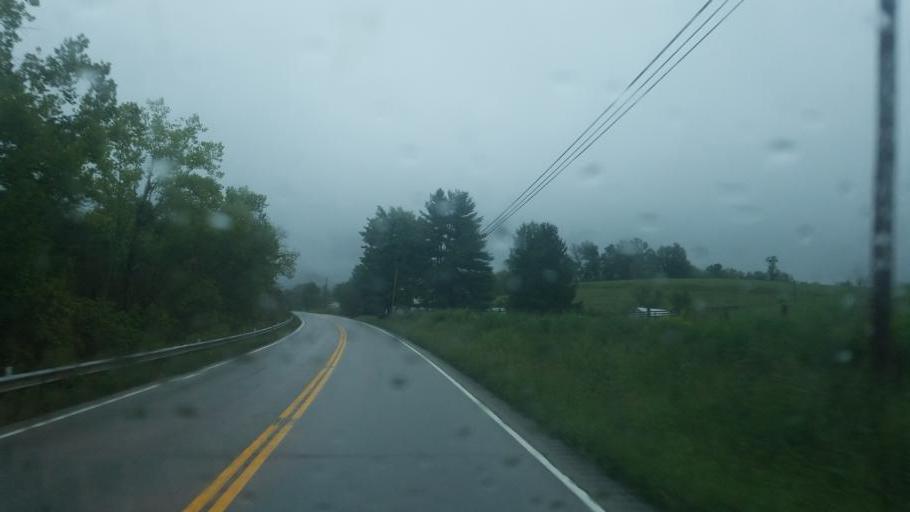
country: US
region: Kentucky
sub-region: Fleming County
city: Flemingsburg
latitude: 38.3715
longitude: -83.6291
